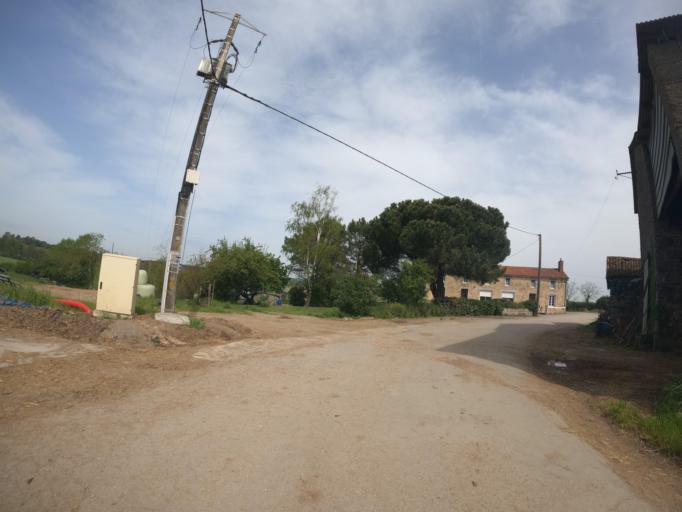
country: FR
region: Poitou-Charentes
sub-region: Departement des Deux-Sevres
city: La Chapelle-Saint-Laurent
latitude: 46.7022
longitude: -0.5071
